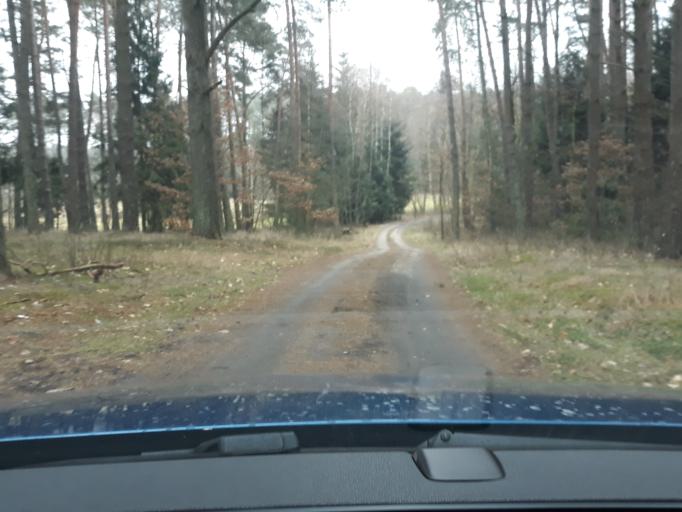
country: PL
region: Pomeranian Voivodeship
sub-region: Powiat czluchowski
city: Czluchow
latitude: 53.8251
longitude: 17.4258
